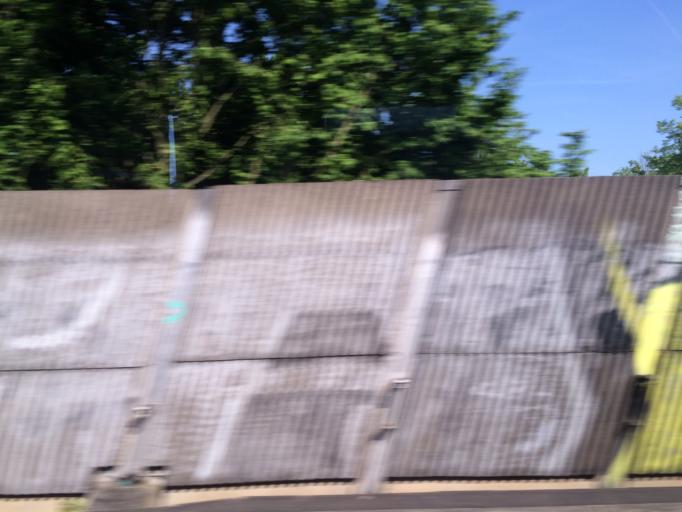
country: DE
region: North Rhine-Westphalia
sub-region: Regierungsbezirk Dusseldorf
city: Dusseldorf
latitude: 51.2745
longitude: 6.7890
